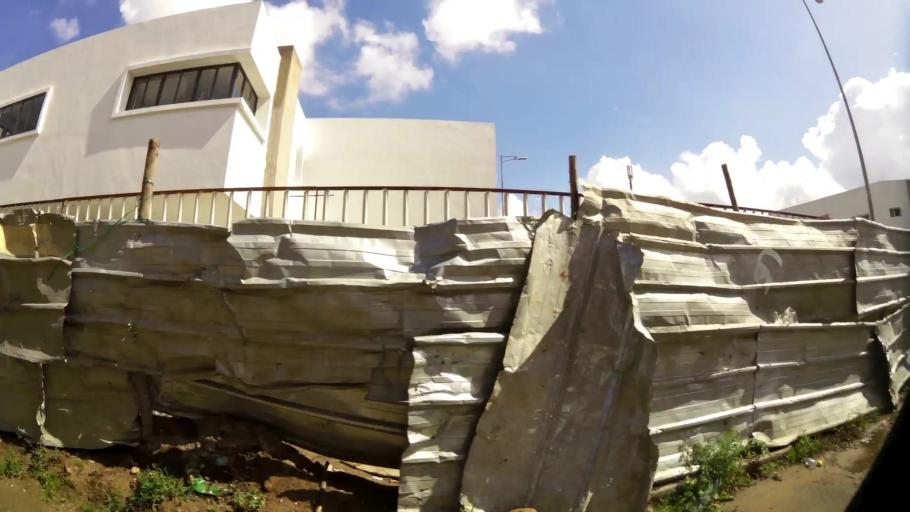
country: MA
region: Grand Casablanca
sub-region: Mediouna
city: Tit Mellil
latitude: 33.5500
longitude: -7.4873
